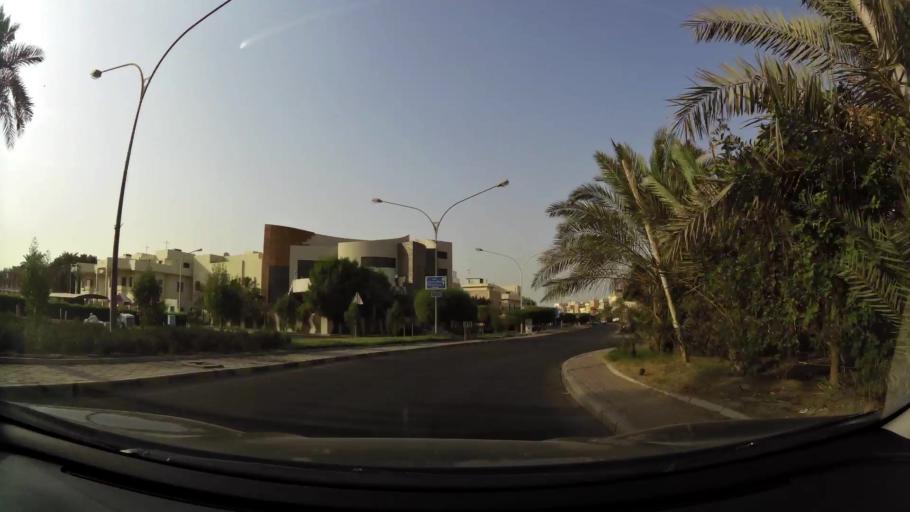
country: KW
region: Muhafazat Hawalli
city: Hawalli
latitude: 29.3067
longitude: 48.0092
